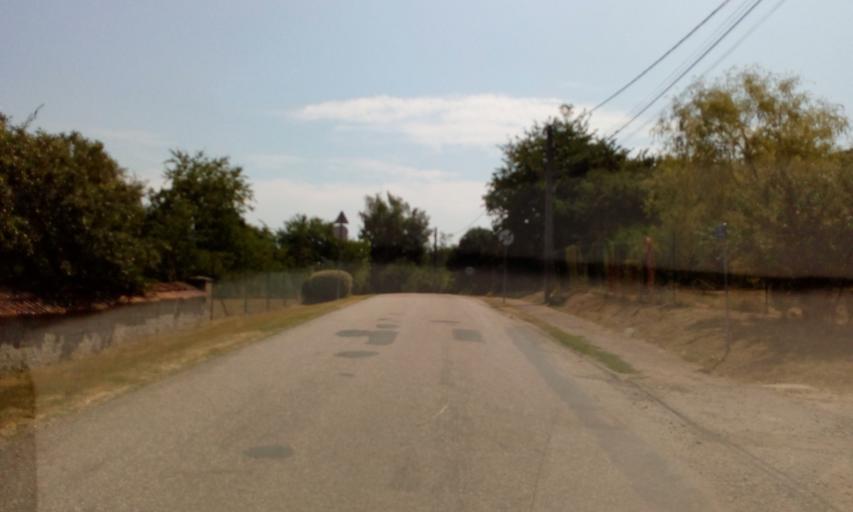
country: FR
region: Lorraine
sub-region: Departement de la Meuse
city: Etain
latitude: 49.1290
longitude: 5.5530
